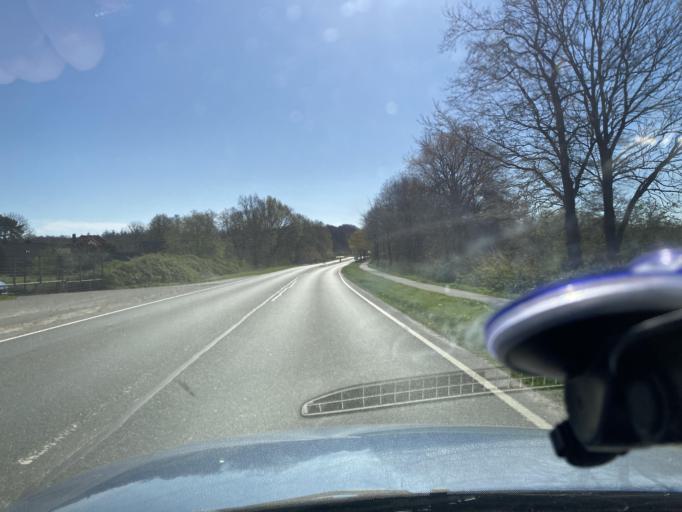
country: DE
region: Schleswig-Holstein
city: Nordhastedt
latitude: 54.1752
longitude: 9.1860
